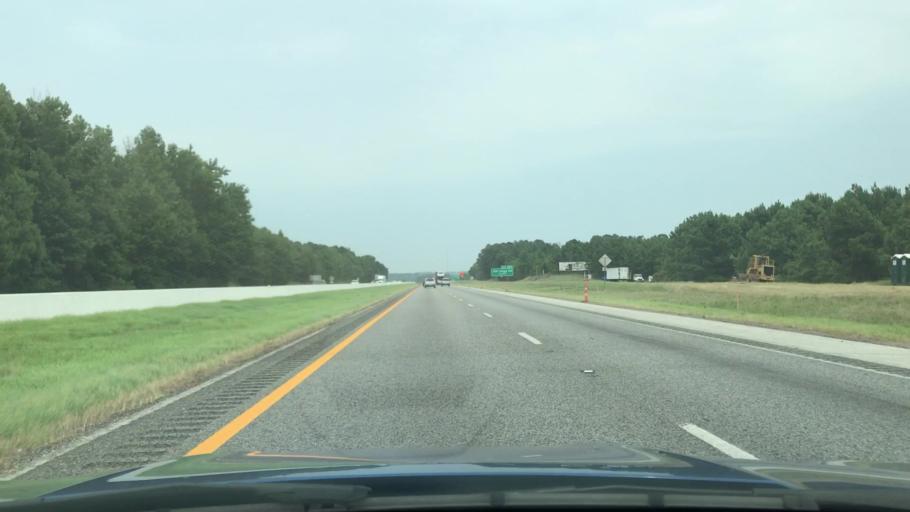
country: US
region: Texas
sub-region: Smith County
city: Lindale
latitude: 32.4683
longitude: -95.3795
